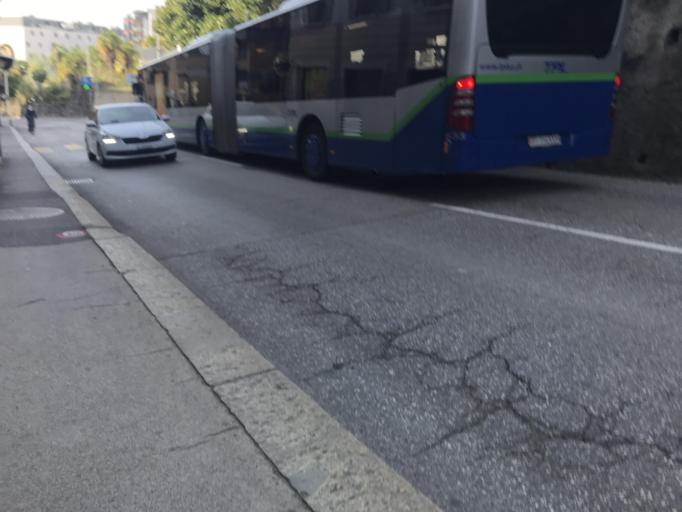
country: CH
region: Ticino
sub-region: Lugano District
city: Massagno
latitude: 46.0111
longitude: 8.9468
